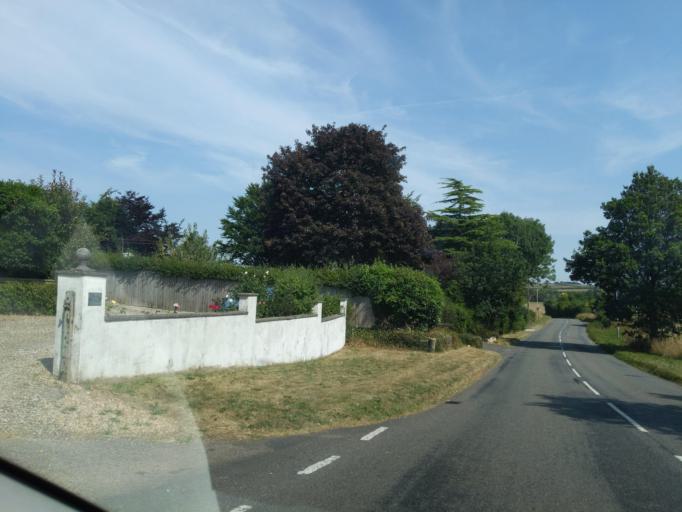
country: GB
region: England
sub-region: Devon
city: Okehampton
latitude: 50.7972
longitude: -3.9845
